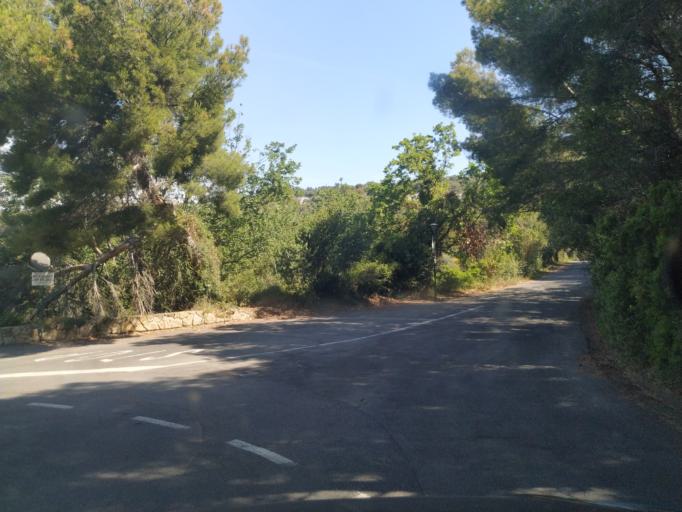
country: IT
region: Liguria
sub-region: Provincia di Savona
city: Marina di Andora
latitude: 43.9580
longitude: 8.1573
